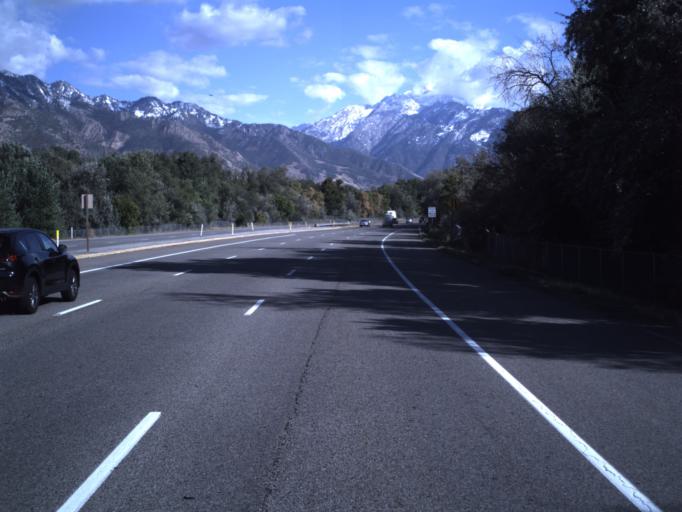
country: US
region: Utah
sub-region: Salt Lake County
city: Millcreek
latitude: 40.6649
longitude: -111.8624
